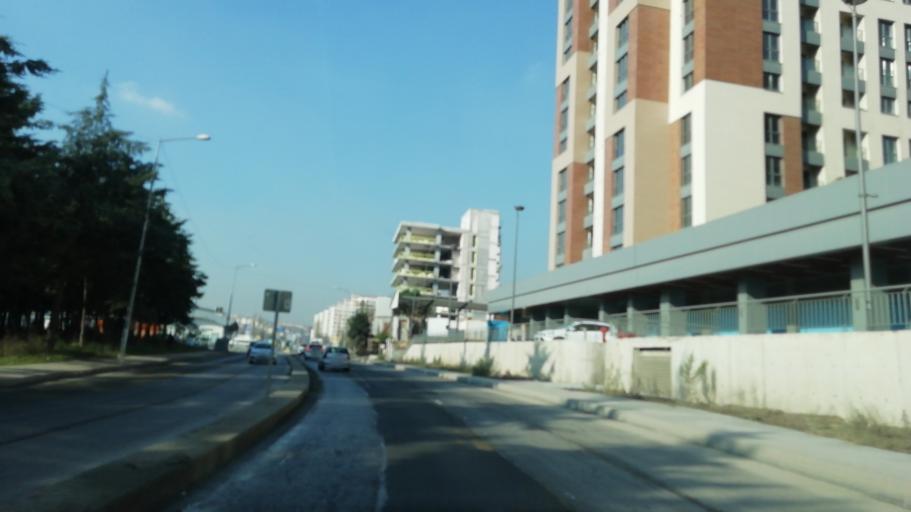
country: TR
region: Istanbul
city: Sisli
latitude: 41.0878
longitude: 28.9484
